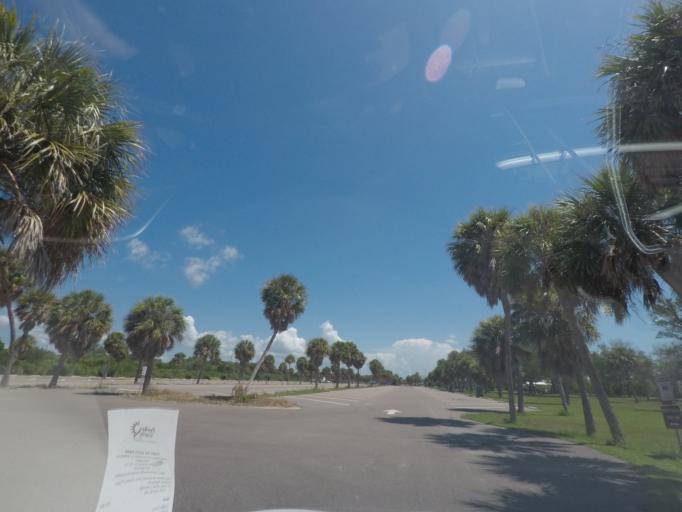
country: US
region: Florida
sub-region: Pinellas County
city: Tierra Verde
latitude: 27.6415
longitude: -82.7398
